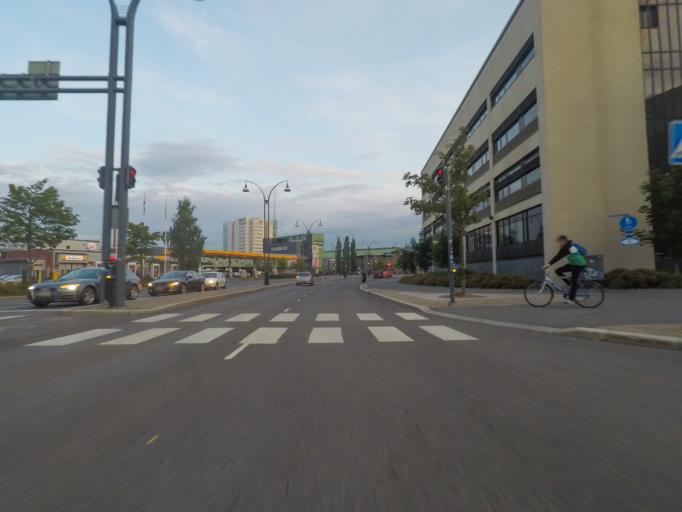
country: FI
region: Central Finland
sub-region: Jyvaeskylae
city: Jyvaeskylae
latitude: 62.2442
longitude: 25.7554
